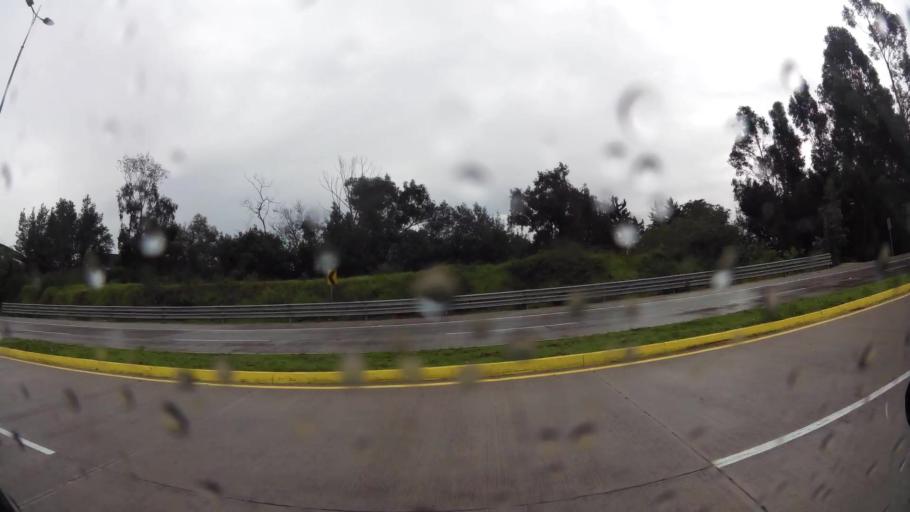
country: EC
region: Pichincha
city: Sangolqui
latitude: -0.2905
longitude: -78.4635
